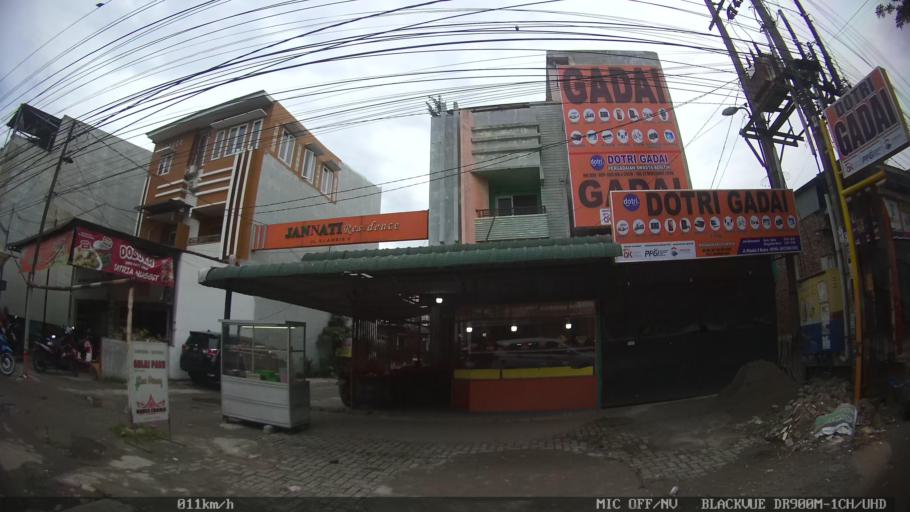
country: ID
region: North Sumatra
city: Sunggal
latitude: 3.6117
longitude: 98.6072
